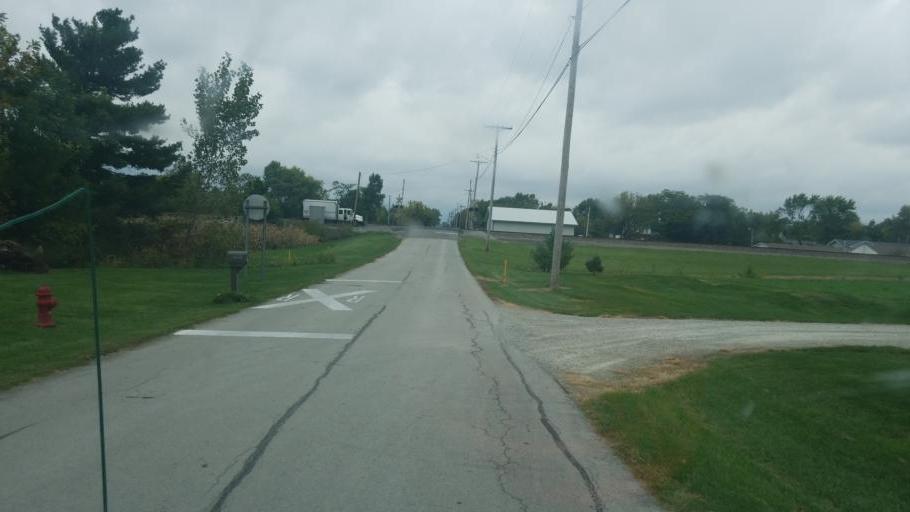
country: US
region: Ohio
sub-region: Seneca County
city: Fostoria
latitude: 41.1115
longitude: -83.5163
